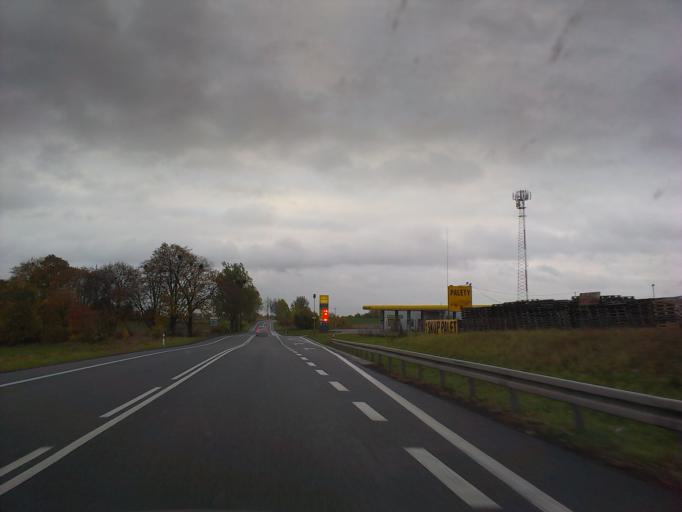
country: PL
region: Kujawsko-Pomorskie
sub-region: Powiat chelminski
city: Chelmno
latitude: 53.3168
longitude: 18.5062
